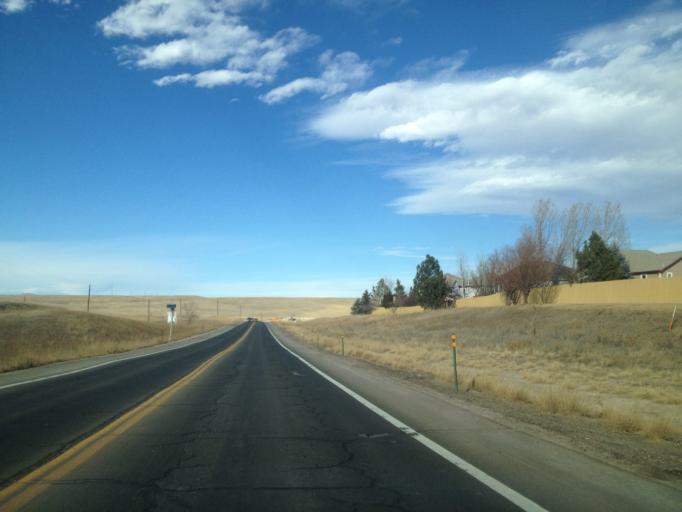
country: US
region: Colorado
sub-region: Boulder County
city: Superior
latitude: 39.9209
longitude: -105.1646
